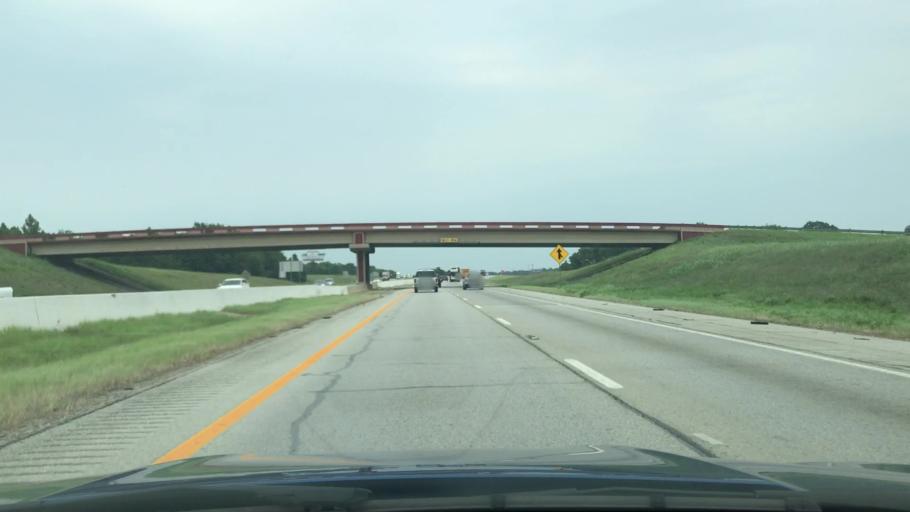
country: US
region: Texas
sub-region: Smith County
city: Hideaway
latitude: 32.4687
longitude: -95.4195
